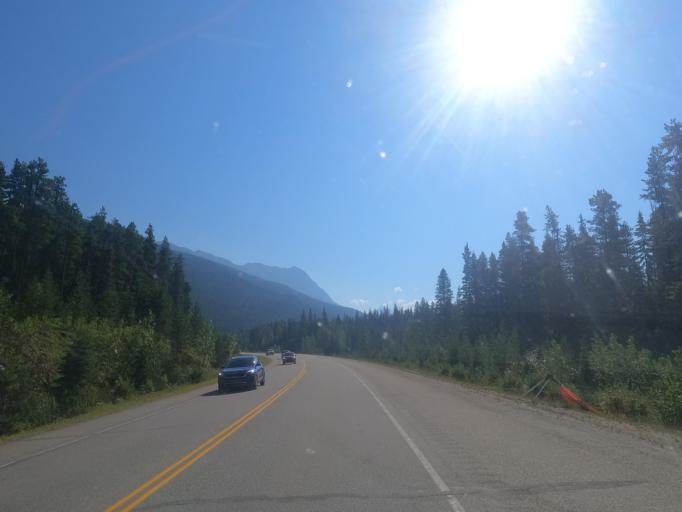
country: CA
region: Alberta
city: Jasper Park Lodge
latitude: 52.8927
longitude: -118.7439
